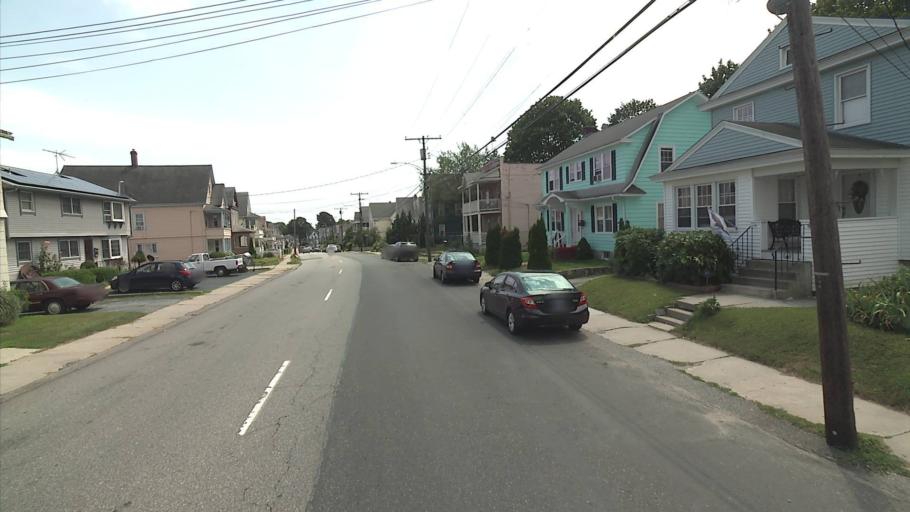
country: US
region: Connecticut
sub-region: New London County
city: New London
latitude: 41.3500
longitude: -72.1113
